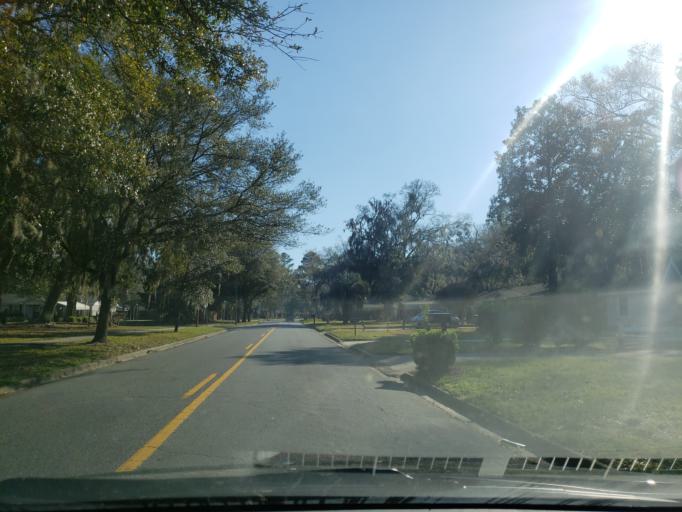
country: US
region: Georgia
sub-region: Chatham County
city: Montgomery
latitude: 31.9887
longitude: -81.1452
